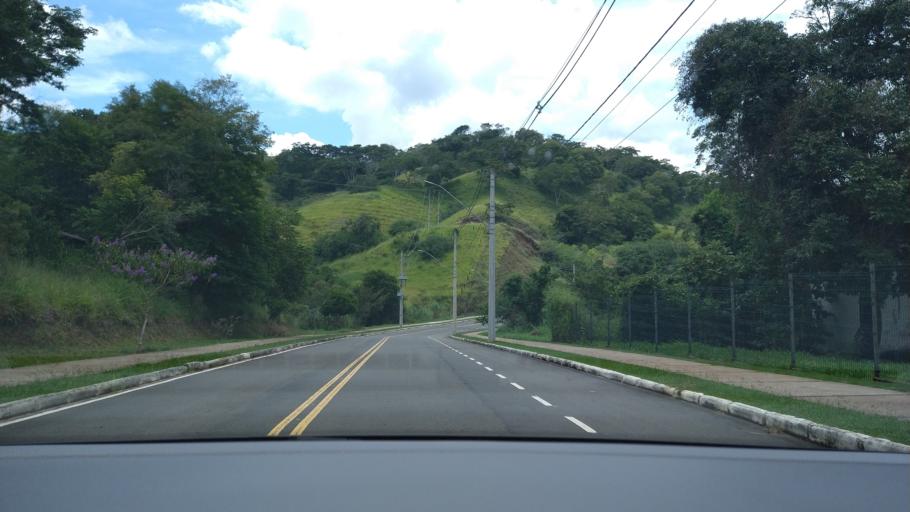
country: BR
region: Minas Gerais
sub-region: Vicosa
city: Vicosa
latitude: -20.7621
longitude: -42.8597
